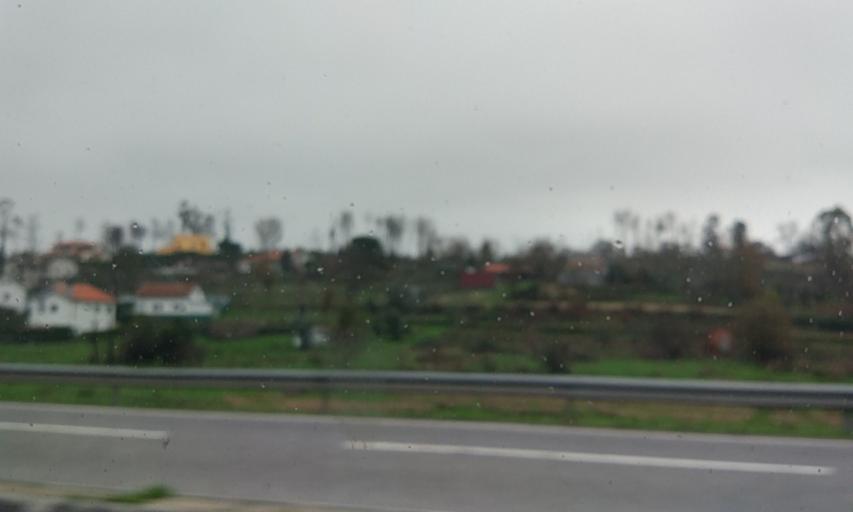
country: PT
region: Viseu
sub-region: Concelho de Tondela
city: Tondela
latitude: 40.5344
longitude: -8.0608
